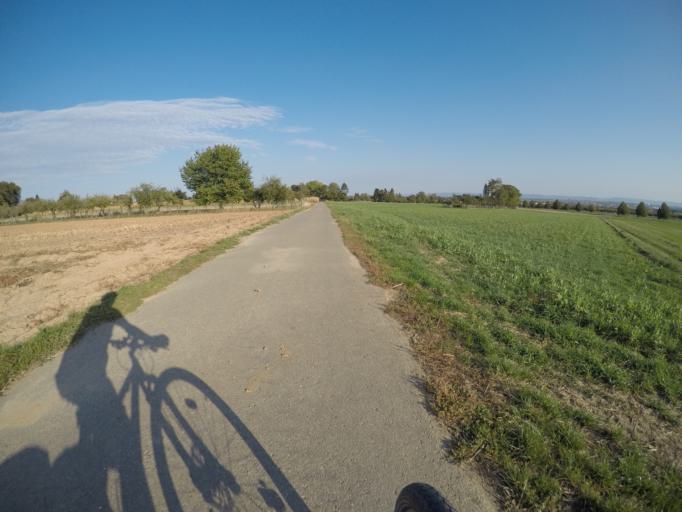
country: DE
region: Baden-Wuerttemberg
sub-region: Regierungsbezirk Stuttgart
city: Leinfelden-Echterdingen
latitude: 48.7204
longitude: 9.1896
